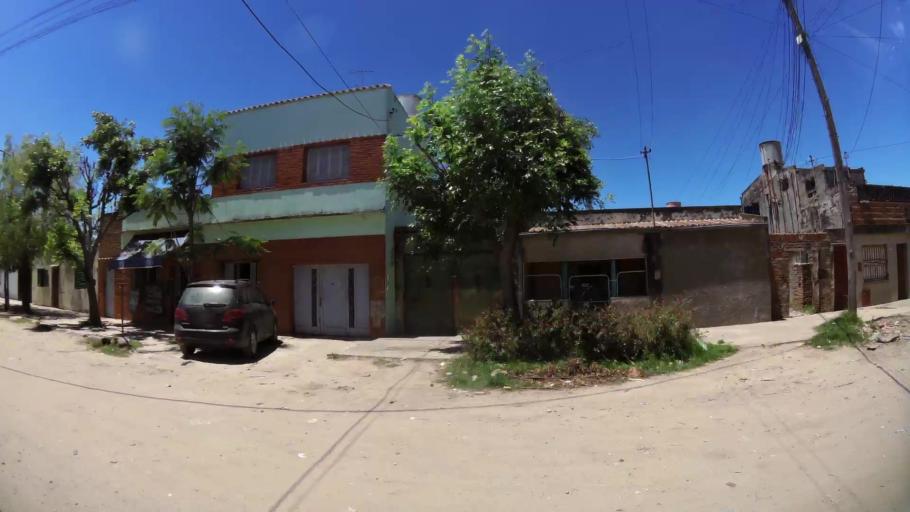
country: AR
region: Santa Fe
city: Santa Fe de la Vera Cruz
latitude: -31.6558
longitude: -60.7273
